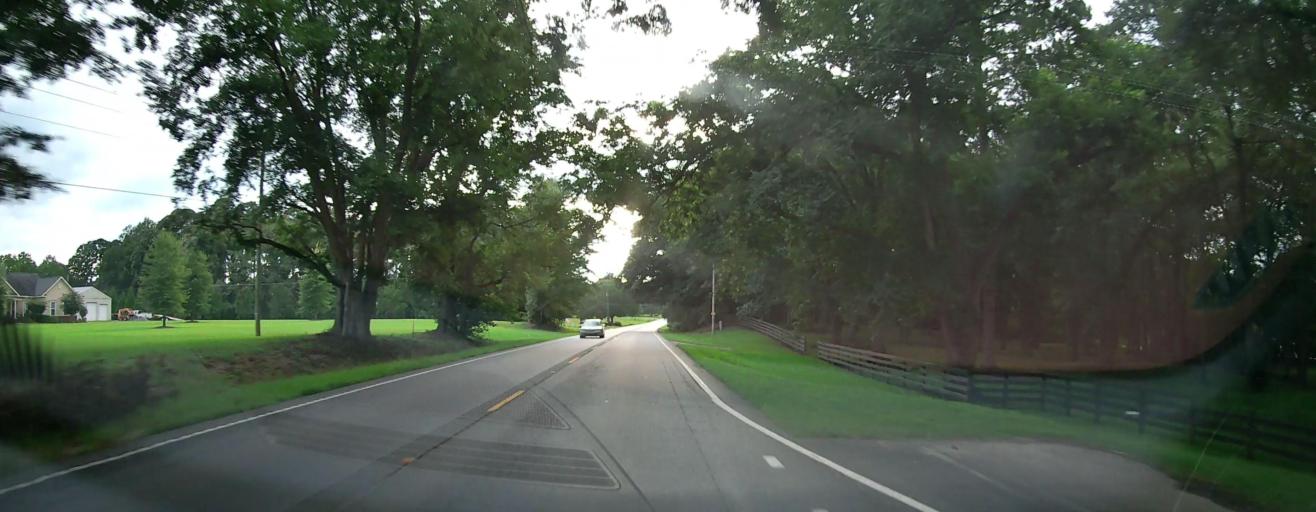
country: US
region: Georgia
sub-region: Houston County
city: Perry
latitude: 32.4526
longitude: -83.6767
